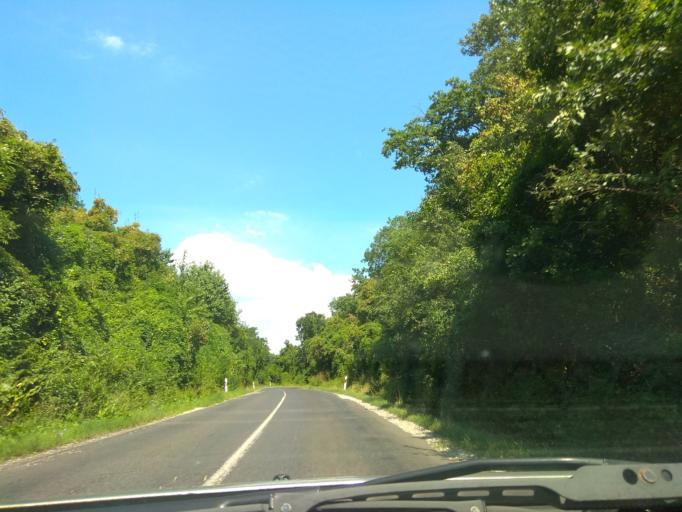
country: HU
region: Borsod-Abauj-Zemplen
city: Harsany
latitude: 48.0223
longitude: 20.7627
